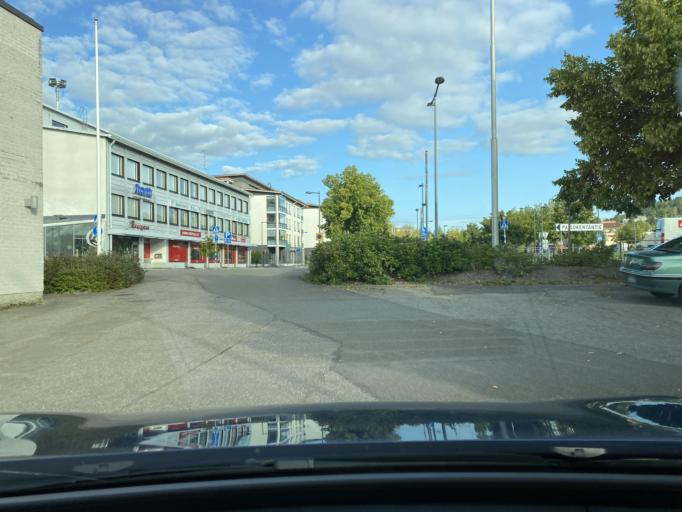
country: FI
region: Kymenlaakso
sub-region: Kouvola
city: Kouvola
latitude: 60.9059
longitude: 26.6252
